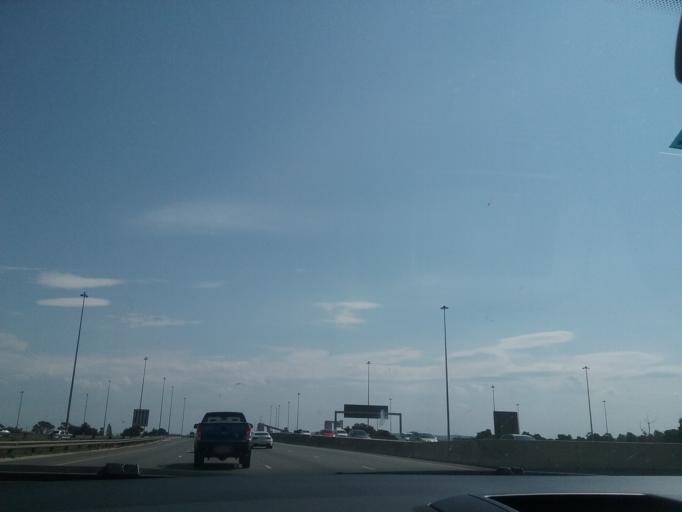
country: ZA
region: Gauteng
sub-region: Ekurhuleni Metropolitan Municipality
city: Germiston
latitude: -26.2107
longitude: 28.1358
